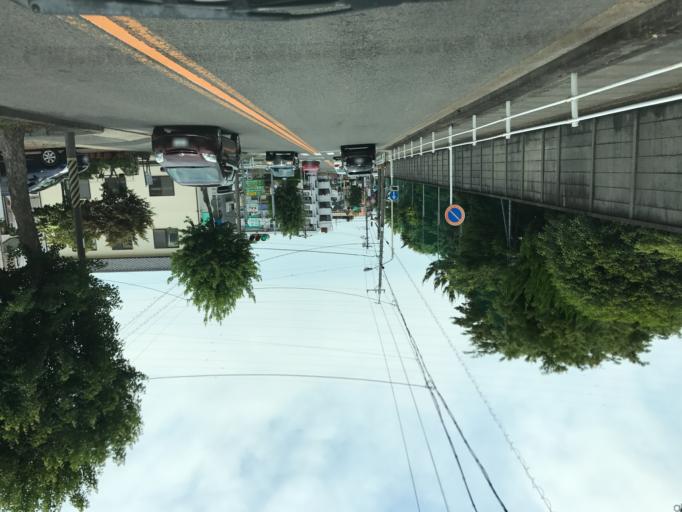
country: JP
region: Aichi
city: Nagoya-shi
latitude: 35.1229
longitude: 136.9613
